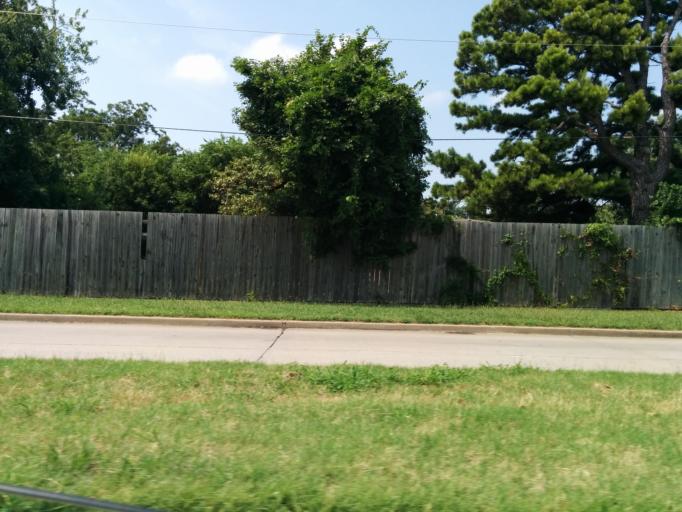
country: US
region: Oklahoma
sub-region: Tulsa County
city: Owasso
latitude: 36.1748
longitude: -95.8867
